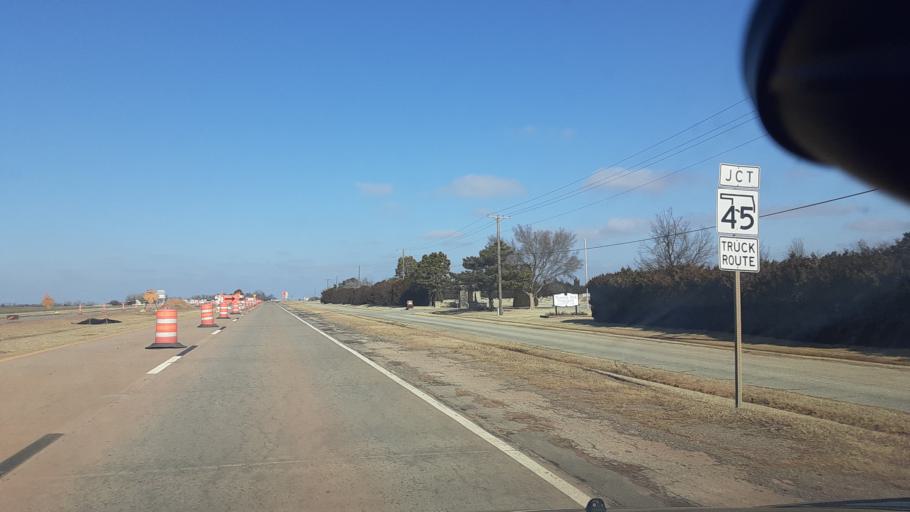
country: US
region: Oklahoma
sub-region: Garfield County
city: Enid
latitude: 36.4569
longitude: -97.8729
